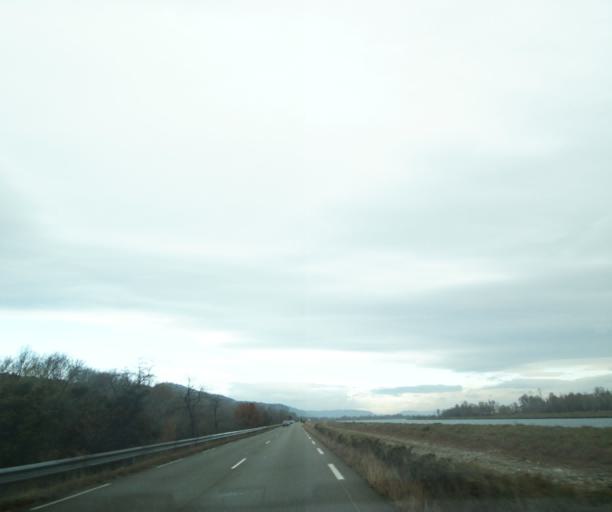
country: FR
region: Rhone-Alpes
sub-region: Departement de l'Ardeche
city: Cornas
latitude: 44.9706
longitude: 4.8599
